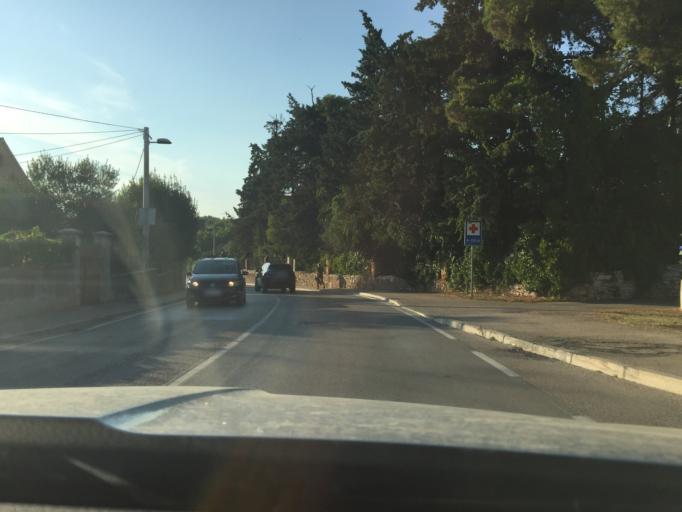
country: HR
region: Zadarska
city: Zadar
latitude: 44.1199
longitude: 15.2348
